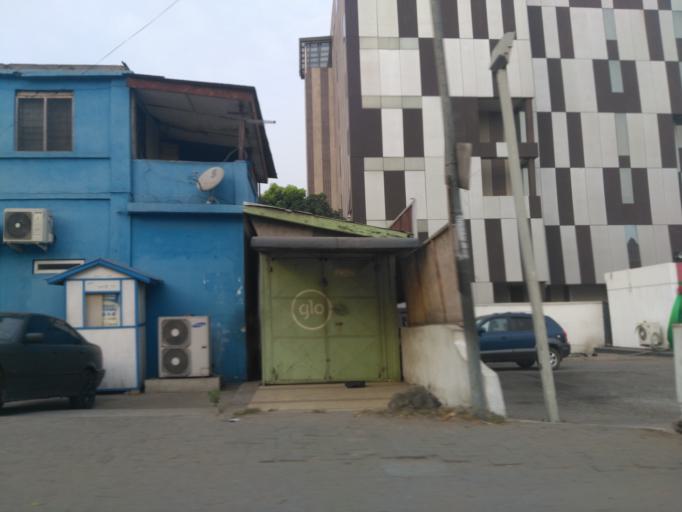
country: GH
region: Greater Accra
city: Accra
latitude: 5.5664
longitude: -0.2148
